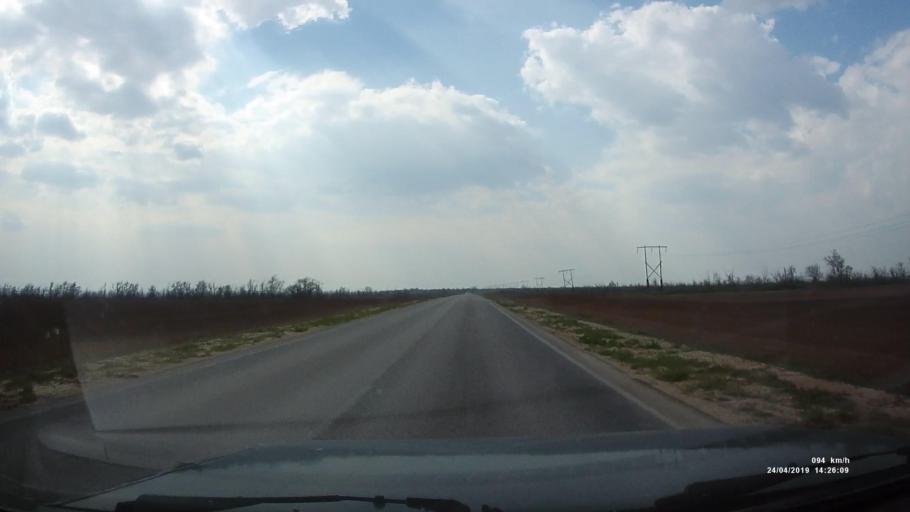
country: RU
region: Kalmykiya
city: Arshan'
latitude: 46.3329
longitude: 44.0681
